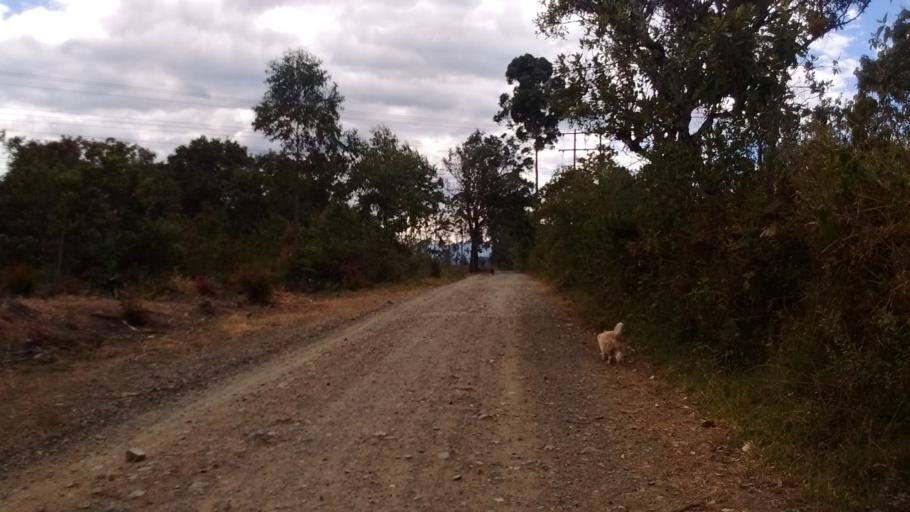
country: CO
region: Cauca
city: Popayan
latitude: 2.4940
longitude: -76.5887
